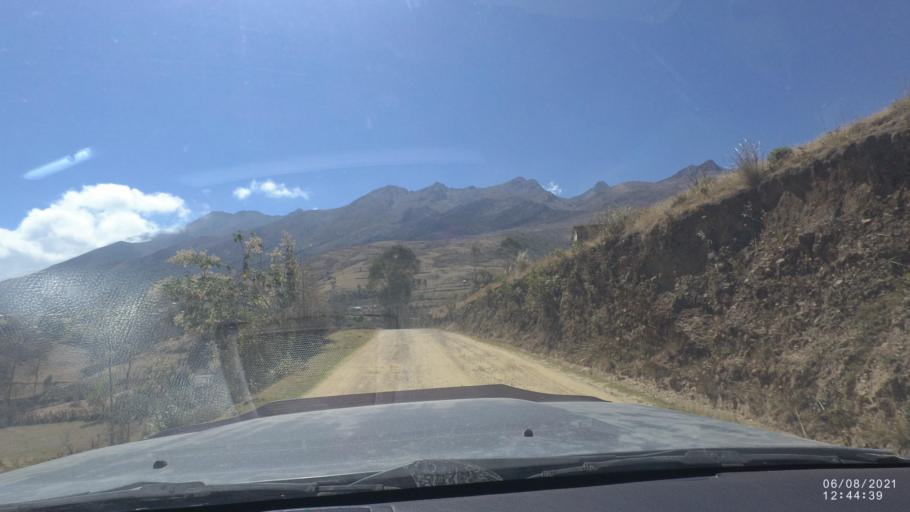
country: BO
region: Cochabamba
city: Colchani
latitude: -16.7681
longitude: -66.6651
